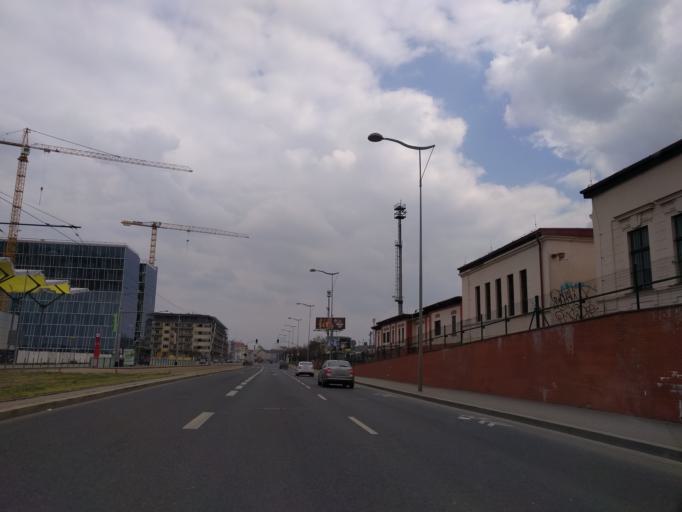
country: CZ
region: Praha
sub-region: Praha 8
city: Liben
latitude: 50.1030
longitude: 14.4925
